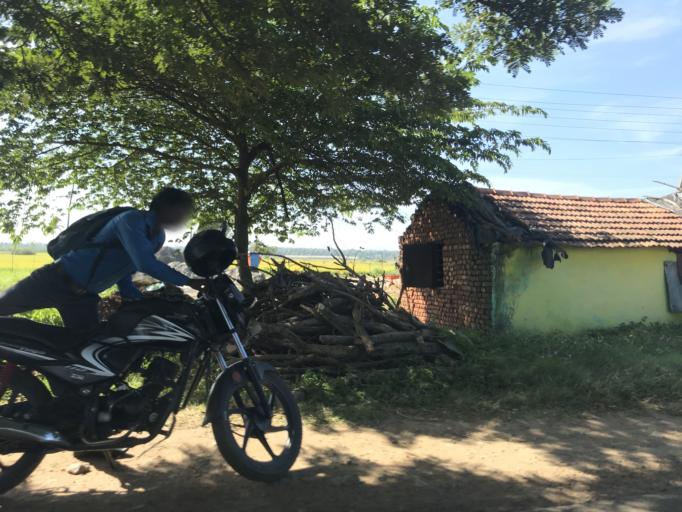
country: IN
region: Karnataka
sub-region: Mysore
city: Heggadadevankote
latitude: 12.1258
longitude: 76.4574
